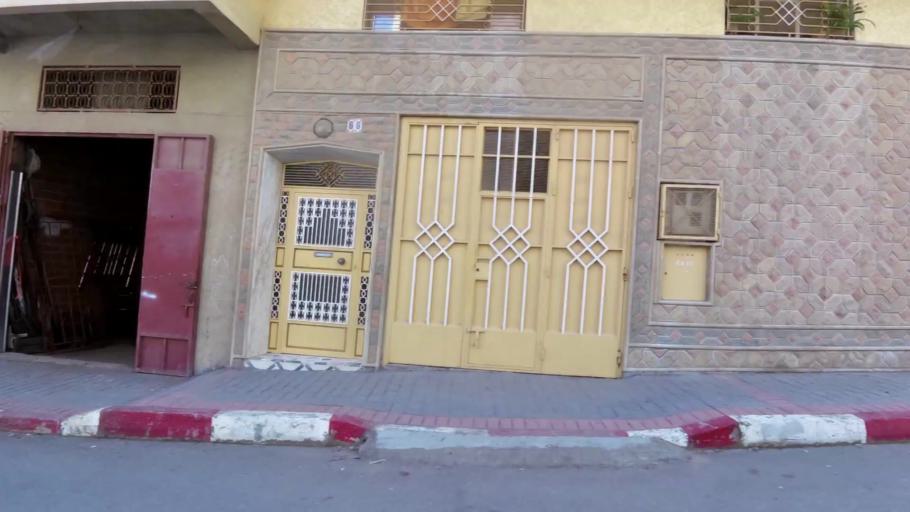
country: MA
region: Tanger-Tetouan
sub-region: Tanger-Assilah
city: Tangier
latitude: 35.7345
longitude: -5.8034
